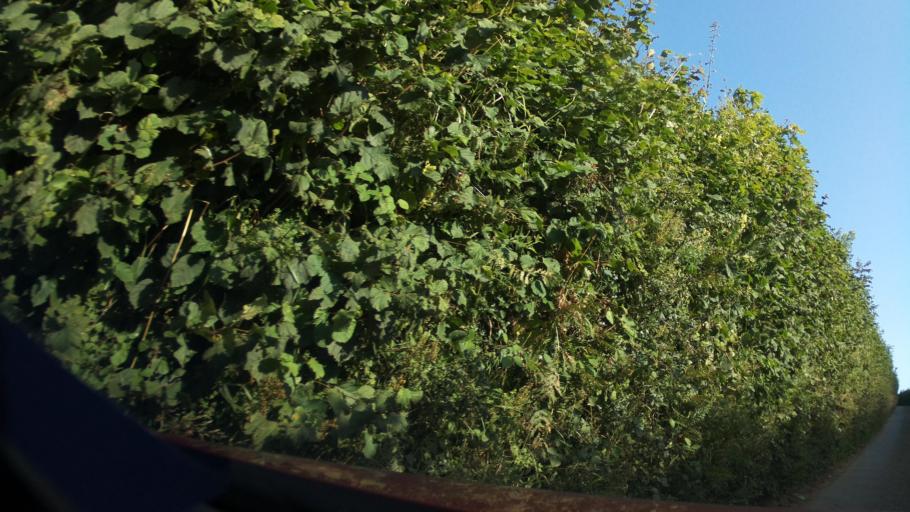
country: GB
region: England
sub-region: Devon
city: Totnes
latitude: 50.4252
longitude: -3.7303
